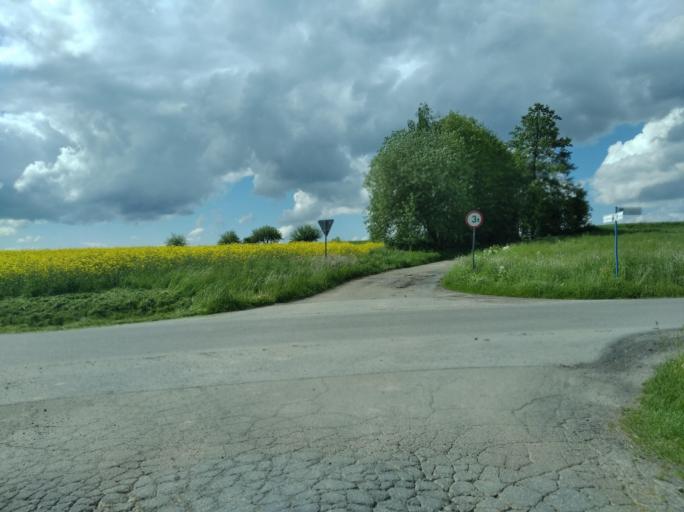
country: PL
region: Subcarpathian Voivodeship
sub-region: Powiat krosnienski
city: Korczyna
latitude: 49.7162
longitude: 21.8300
